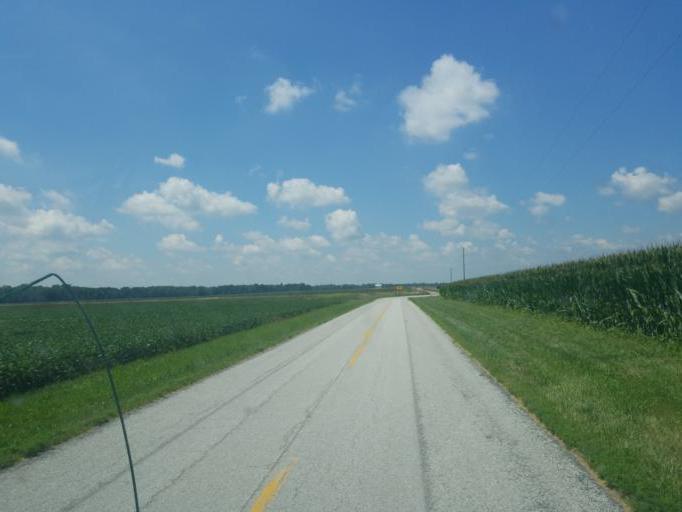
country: US
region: Ohio
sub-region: Allen County
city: Spencerville
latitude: 40.6665
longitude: -84.4335
